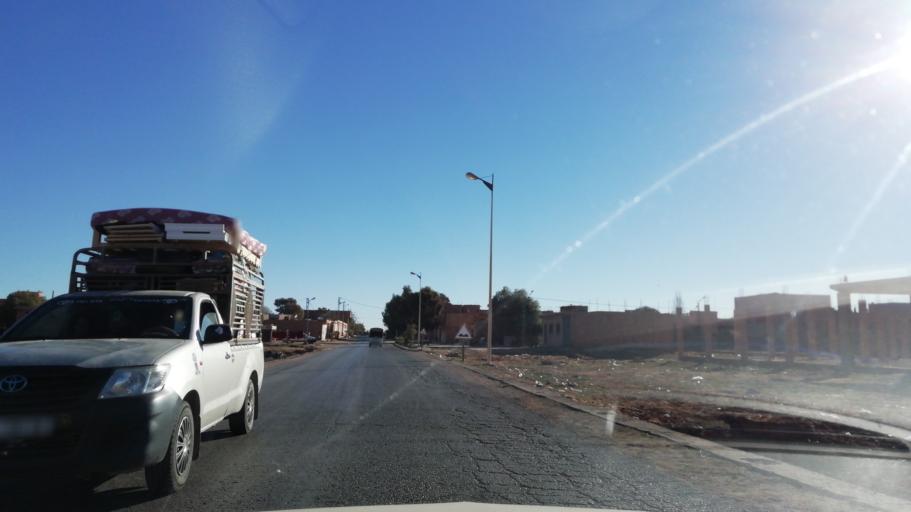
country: DZ
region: El Bayadh
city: El Bayadh
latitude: 33.8531
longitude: 0.6284
